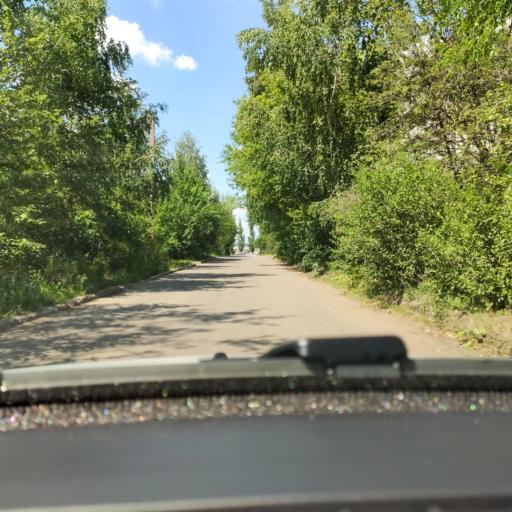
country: RU
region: Voronezj
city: Semiluki
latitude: 51.6945
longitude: 39.0096
